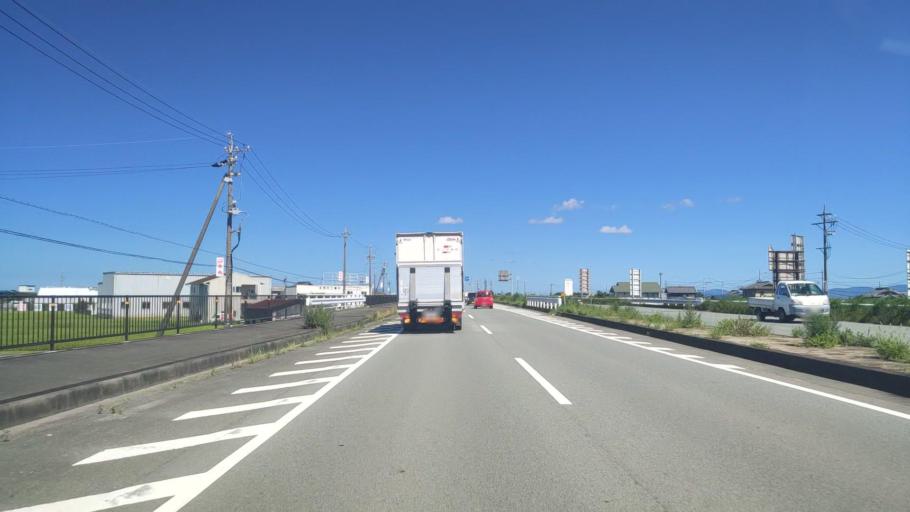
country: JP
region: Mie
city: Hisai-motomachi
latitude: 34.5849
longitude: 136.5575
